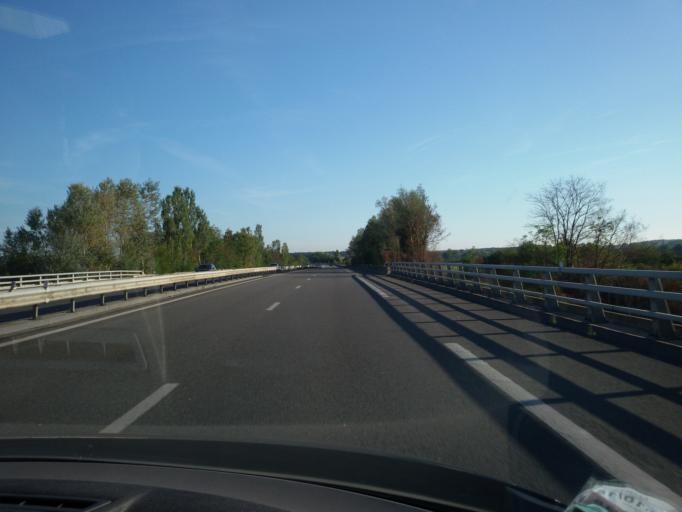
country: FR
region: Centre
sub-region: Departement du Cher
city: Orval
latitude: 46.7779
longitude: 2.4080
